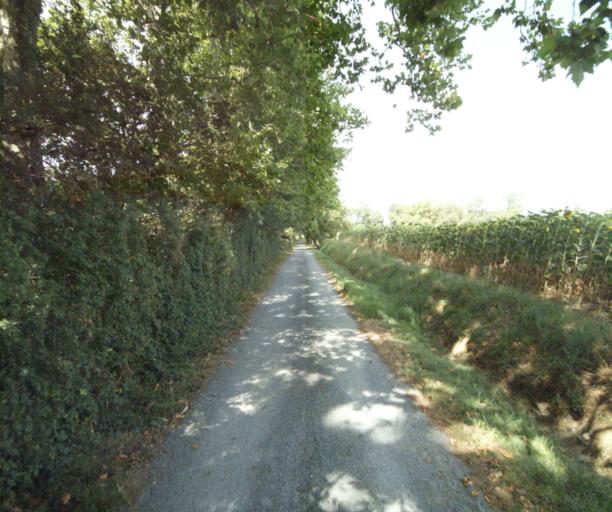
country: FR
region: Midi-Pyrenees
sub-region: Departement du Tarn
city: Soual
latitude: 43.5147
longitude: 2.0730
